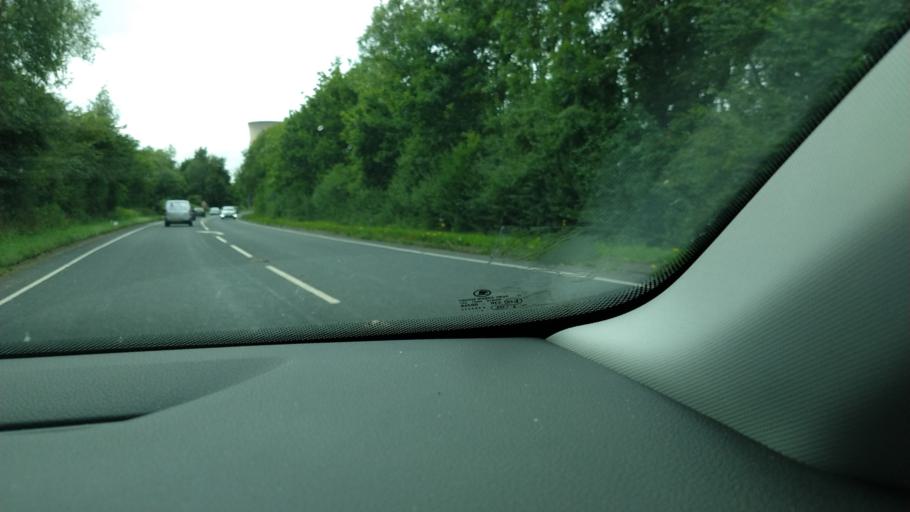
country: GB
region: England
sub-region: North Yorkshire
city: Camblesforth
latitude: 53.7250
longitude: -0.9879
